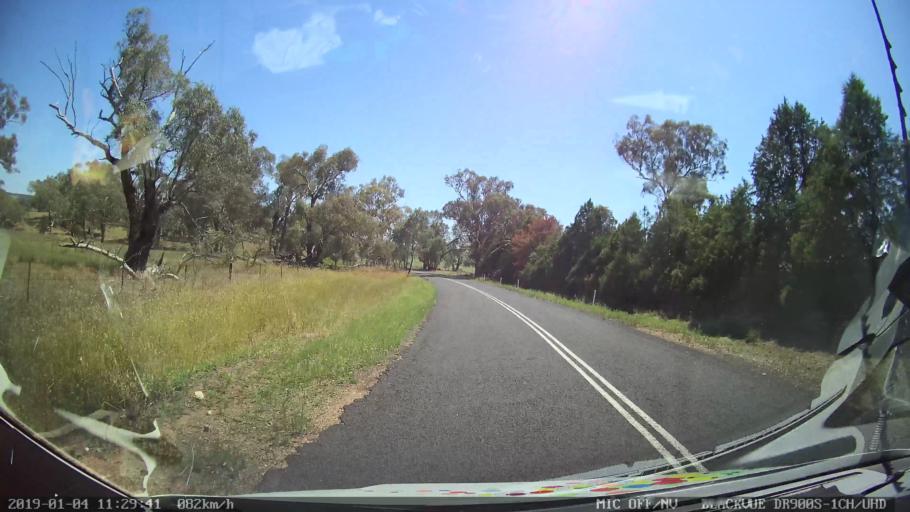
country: AU
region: New South Wales
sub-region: Cabonne
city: Molong
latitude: -33.0852
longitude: 148.7757
